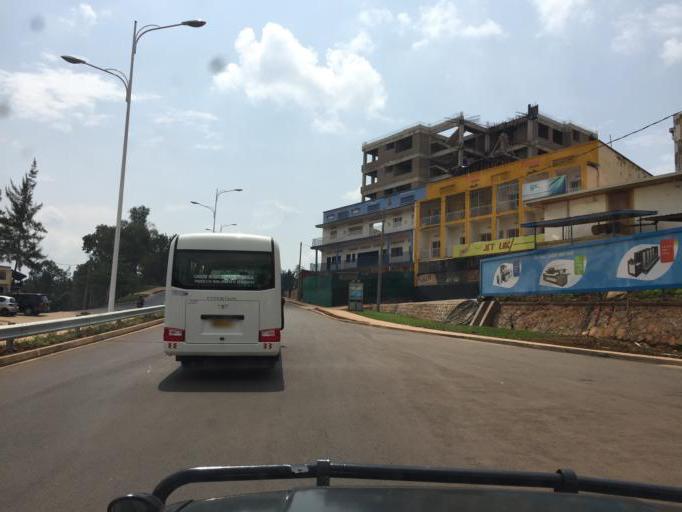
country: RW
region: Kigali
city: Kigali
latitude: -1.9419
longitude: 30.0618
